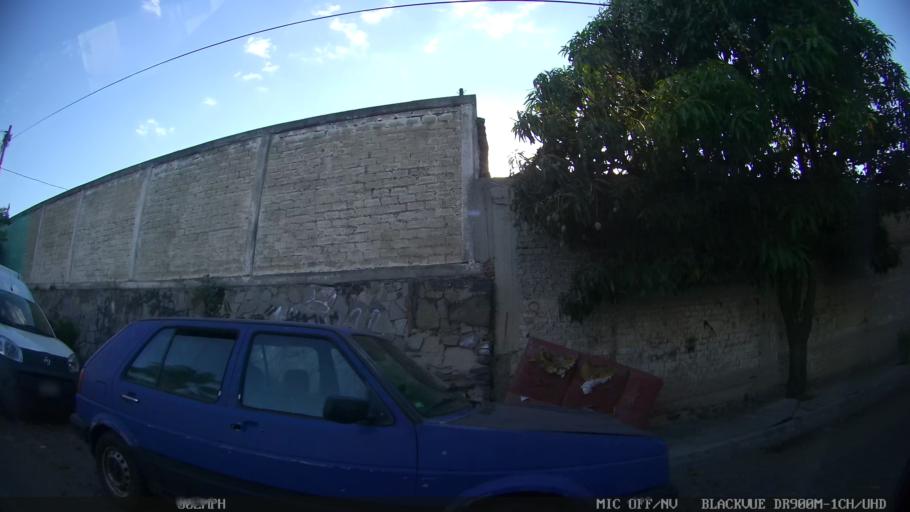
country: MX
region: Jalisco
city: Tlaquepaque
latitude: 20.7075
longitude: -103.3024
